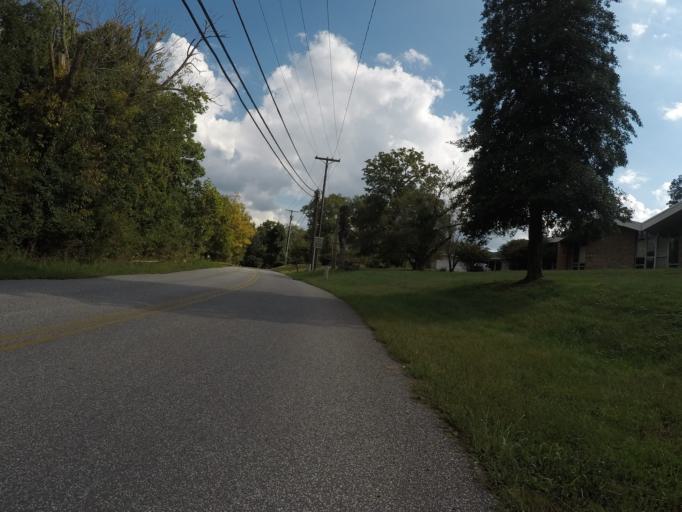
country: US
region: West Virginia
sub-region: Cabell County
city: Huntington
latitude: 38.3967
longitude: -82.4342
